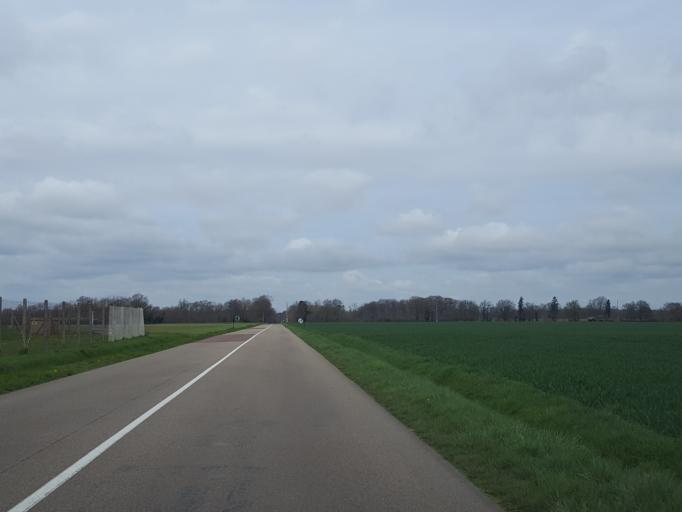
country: FR
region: Centre
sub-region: Departement du Loiret
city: Sainte-Genevieve-des-Bois
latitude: 47.8204
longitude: 2.8303
